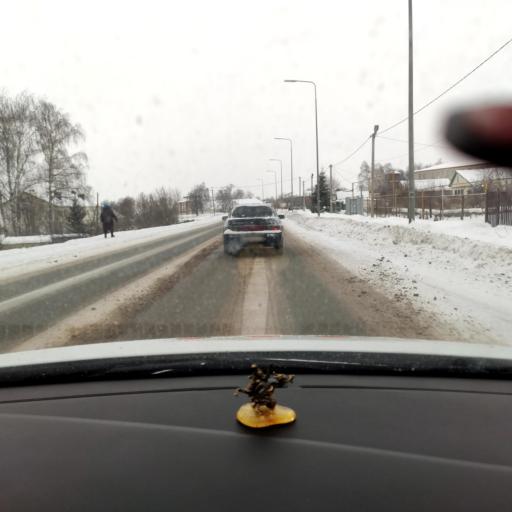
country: RU
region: Tatarstan
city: Vysokaya Gora
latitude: 55.9928
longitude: 49.3094
